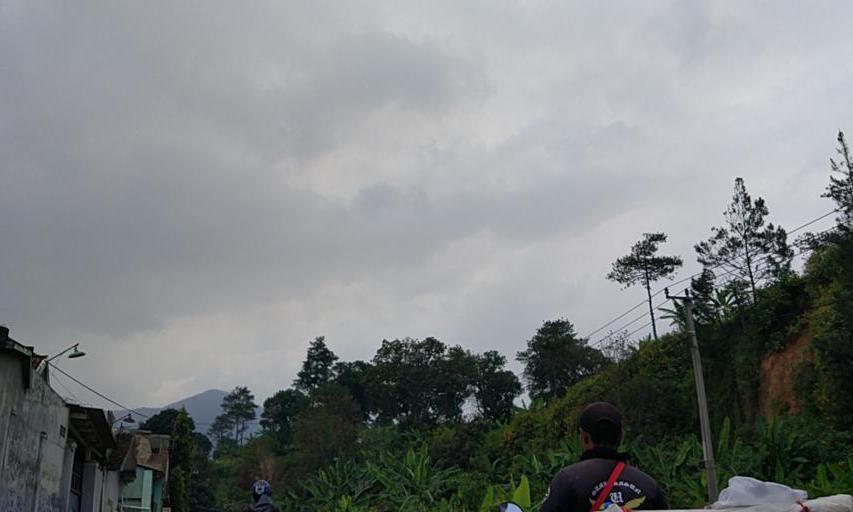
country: ID
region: West Java
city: Bandung
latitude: -6.8848
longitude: 107.6878
